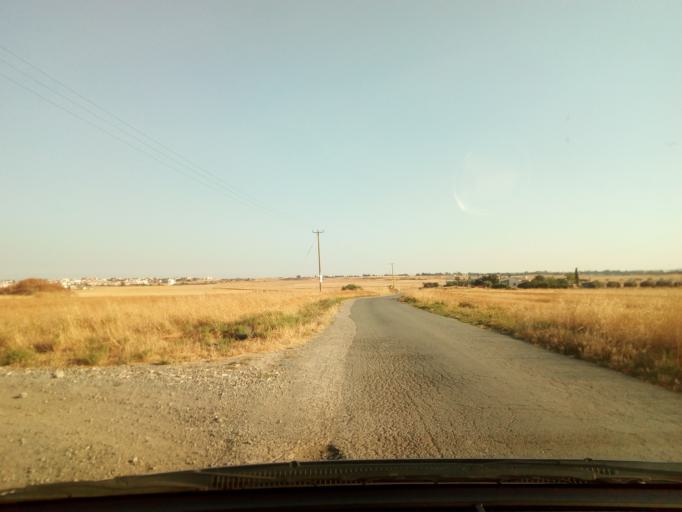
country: CY
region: Larnaka
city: Aradippou
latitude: 34.9259
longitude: 33.5761
